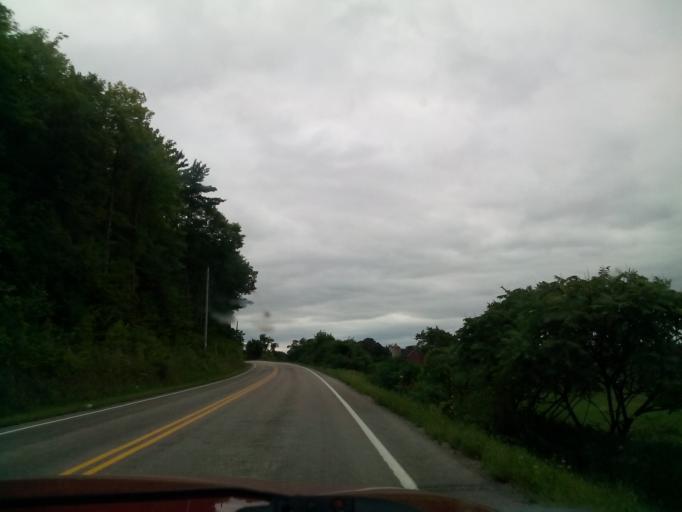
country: US
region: Wisconsin
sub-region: Outagamie County
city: Hortonville
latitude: 44.3473
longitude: -88.6313
